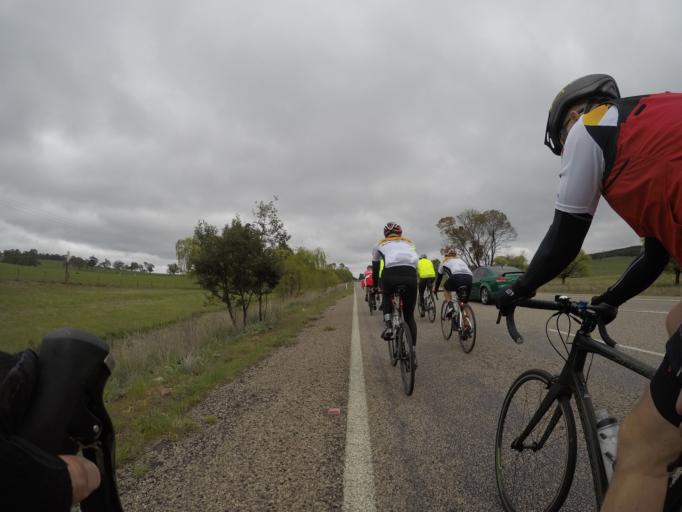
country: AU
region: New South Wales
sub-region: Lithgow
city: Portland
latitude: -33.4332
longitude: 149.9048
